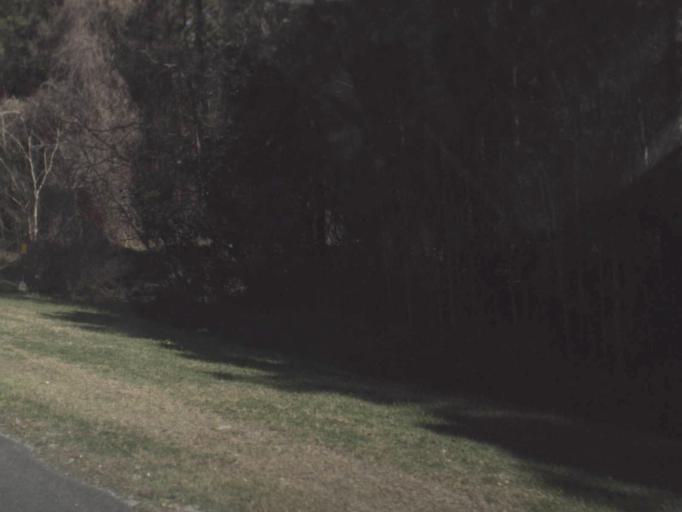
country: US
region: Florida
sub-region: Bay County
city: Hiland Park
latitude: 30.2002
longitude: -85.6496
